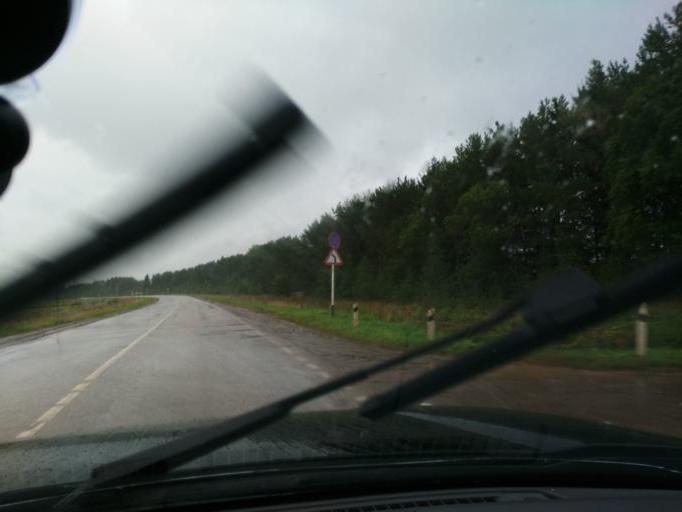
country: RU
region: Perm
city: Osa
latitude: 57.2899
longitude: 55.5898
